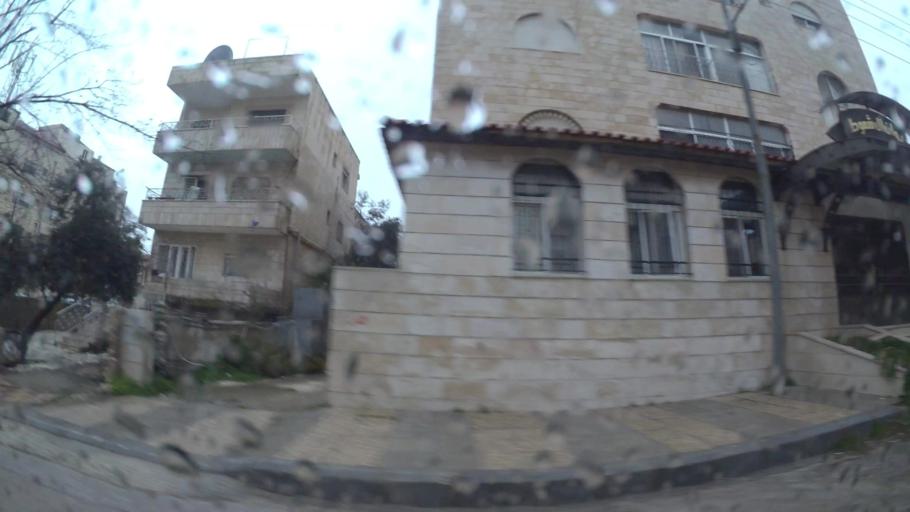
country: JO
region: Amman
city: Al Jubayhah
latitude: 32.0267
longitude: 35.8525
